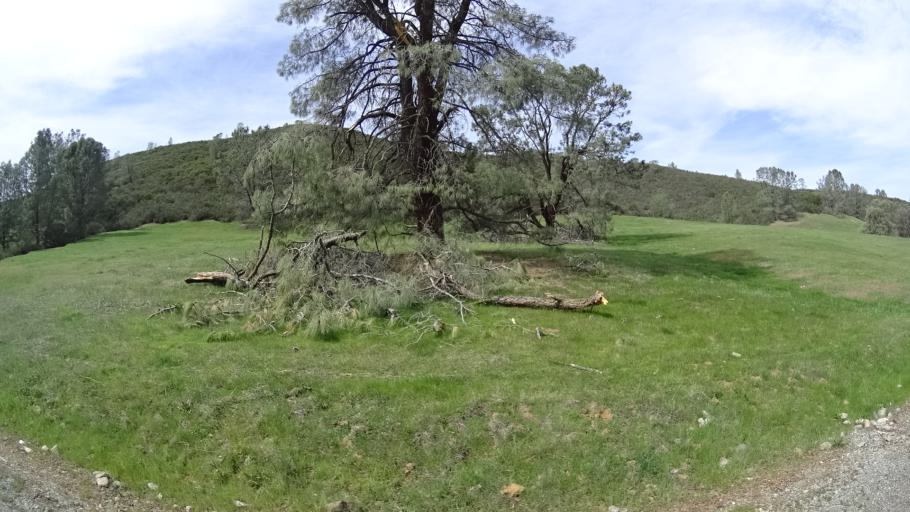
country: US
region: California
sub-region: Glenn County
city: Willows
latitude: 39.5996
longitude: -122.5278
